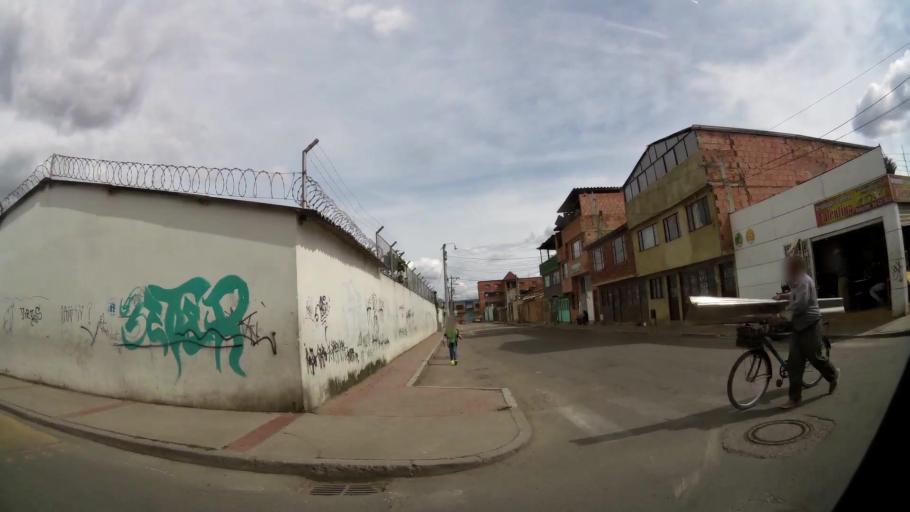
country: CO
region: Cundinamarca
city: Funza
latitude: 4.7075
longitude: -74.2013
